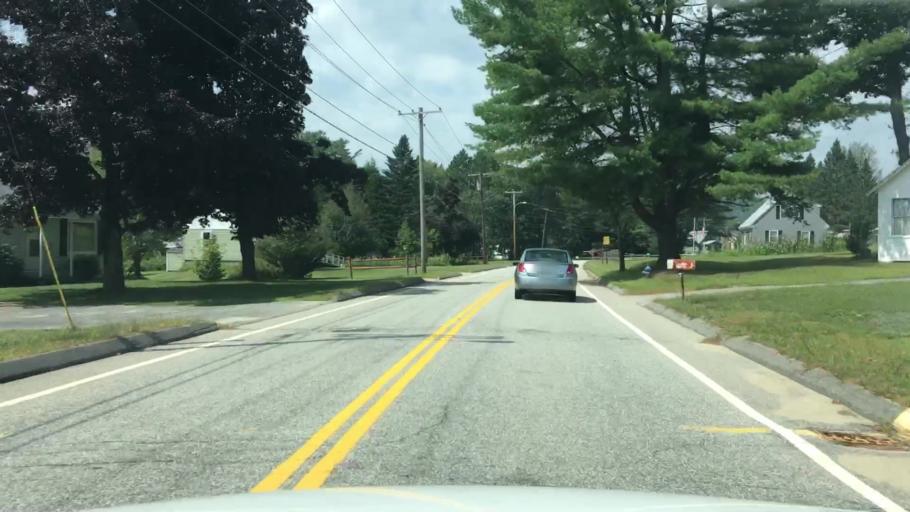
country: US
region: Maine
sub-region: Oxford County
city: Rumford
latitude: 44.5212
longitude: -70.5315
